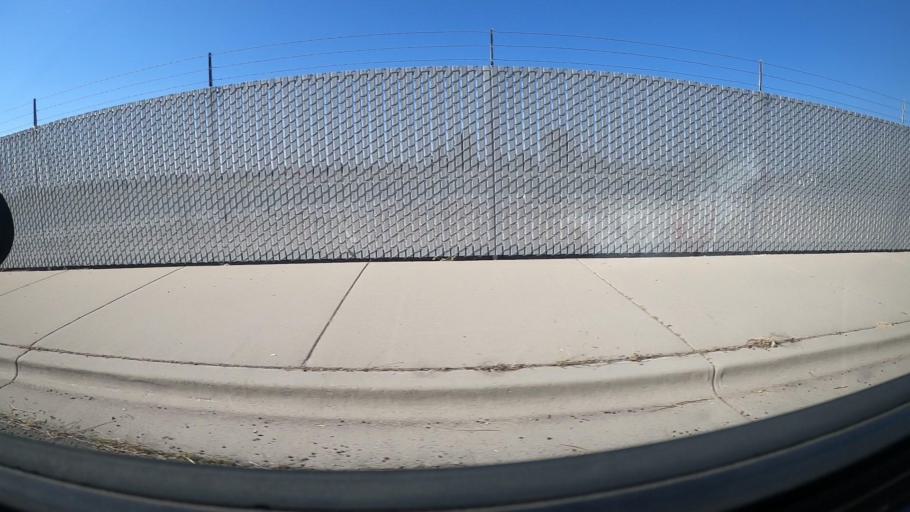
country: US
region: Idaho
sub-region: Ada County
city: Meridian
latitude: 43.5962
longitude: -116.3770
